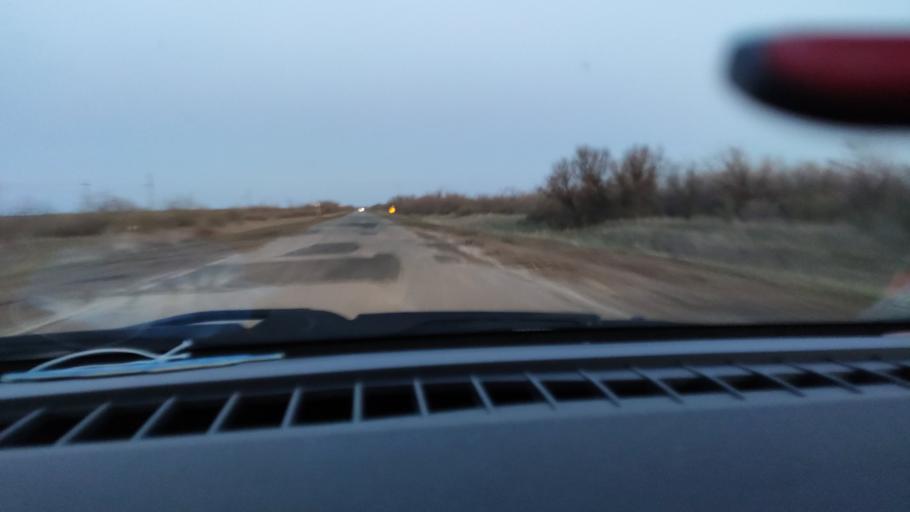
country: RU
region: Saratov
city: Rovnoye
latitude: 51.0535
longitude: 46.0368
